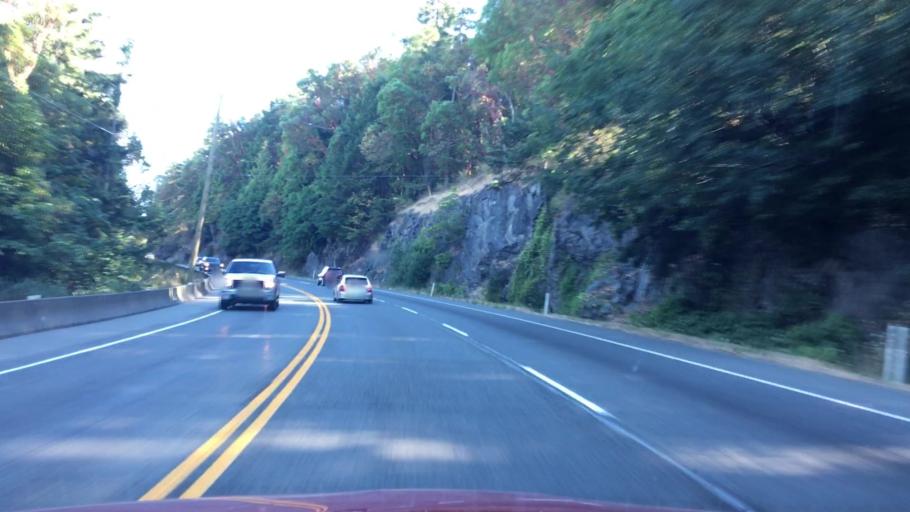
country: CA
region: British Columbia
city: North Saanich
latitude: 48.5947
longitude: -123.5341
